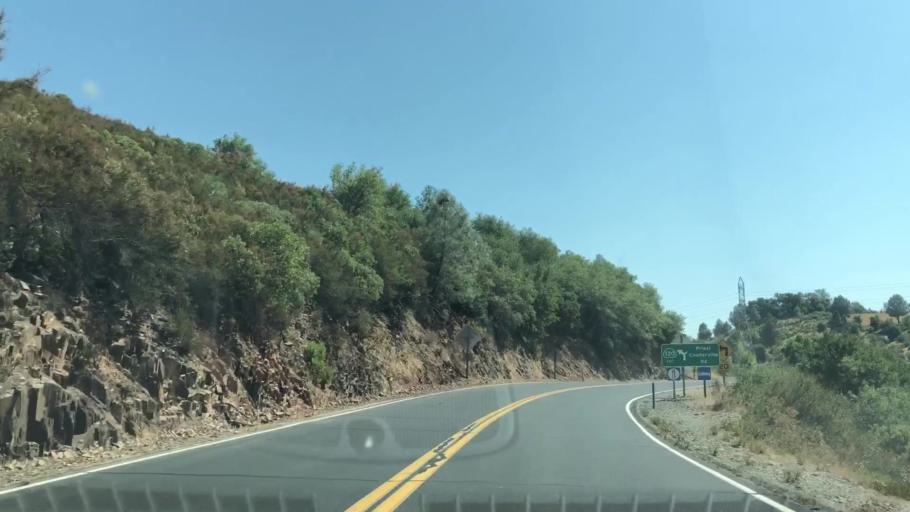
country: US
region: California
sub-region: Tuolumne County
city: Tuolumne City
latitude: 37.8153
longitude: -120.2724
